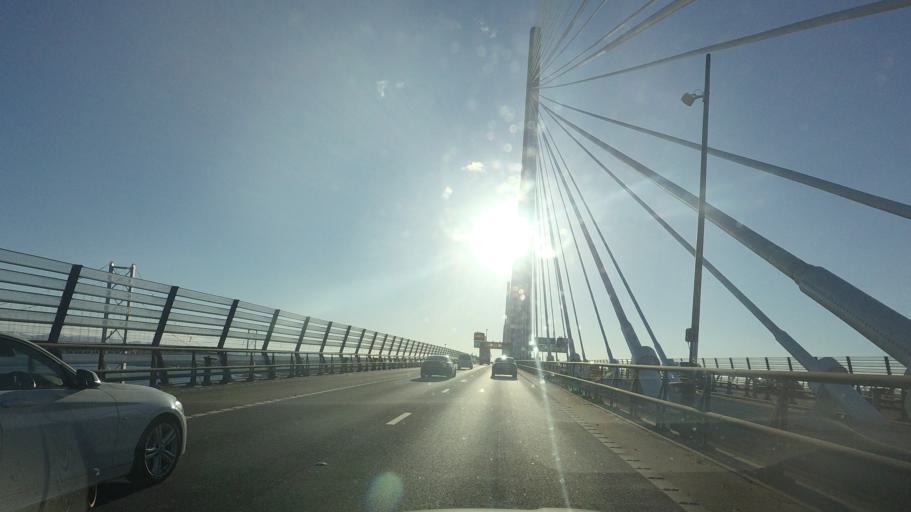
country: GB
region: Scotland
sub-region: Fife
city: North Queensferry
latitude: 56.0124
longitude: -3.4082
